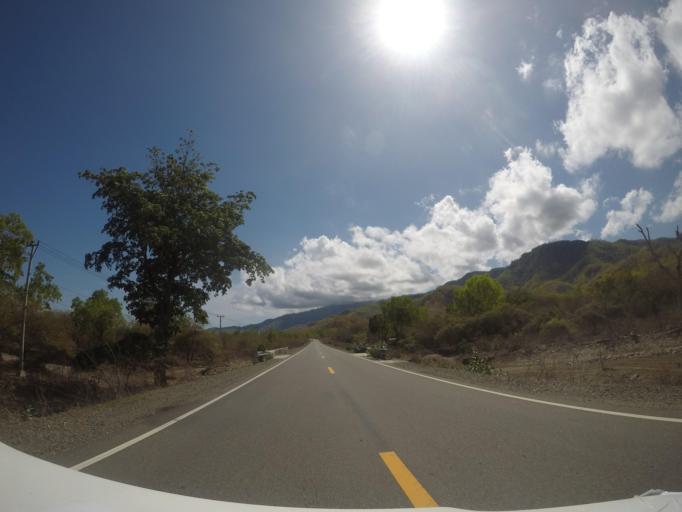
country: ID
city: Metinaro
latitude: -8.5091
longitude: 125.8008
